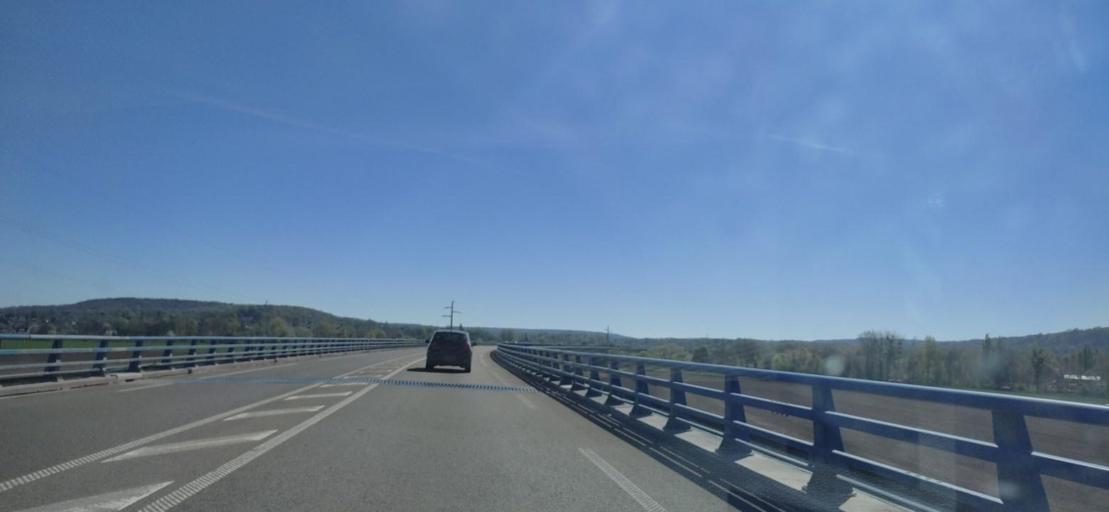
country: FR
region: Picardie
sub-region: Departement de l'Oise
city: Clairoix
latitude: 49.4353
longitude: 2.8576
